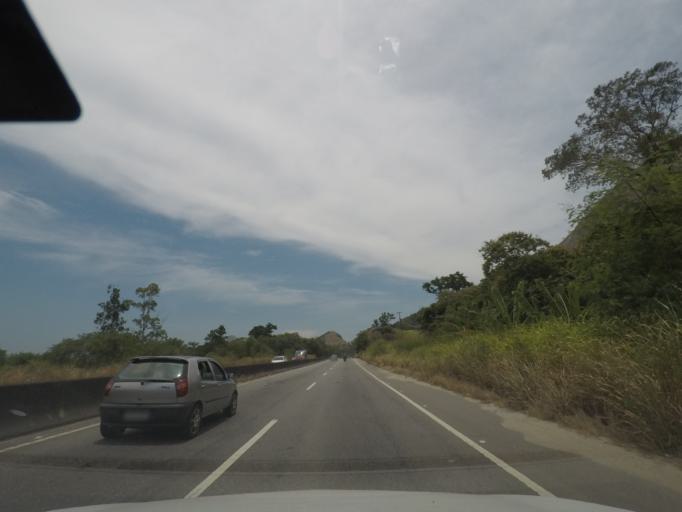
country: BR
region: Rio de Janeiro
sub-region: Marica
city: Marica
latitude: -22.9351
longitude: -42.9106
